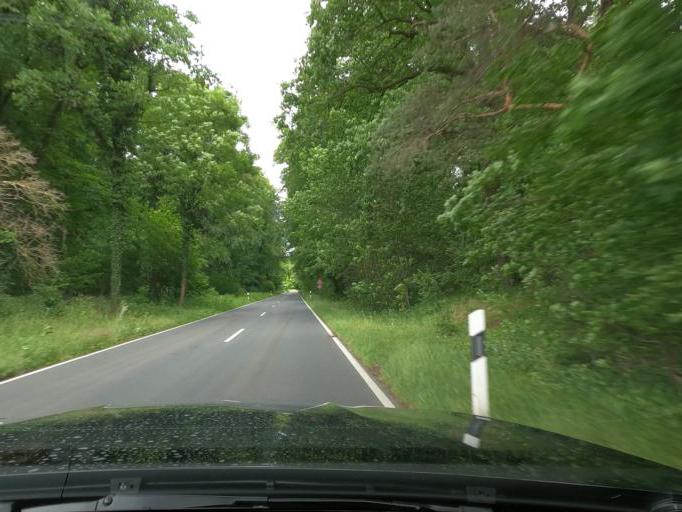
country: DE
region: Lower Saxony
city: Lehrte
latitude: 52.3896
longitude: 9.9231
